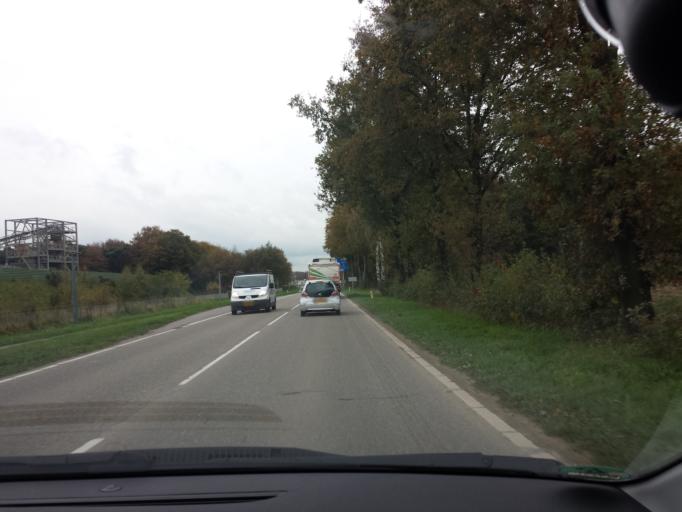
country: NL
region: Limburg
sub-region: Gemeente Beesel
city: Reuver
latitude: 51.2699
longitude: 6.0704
